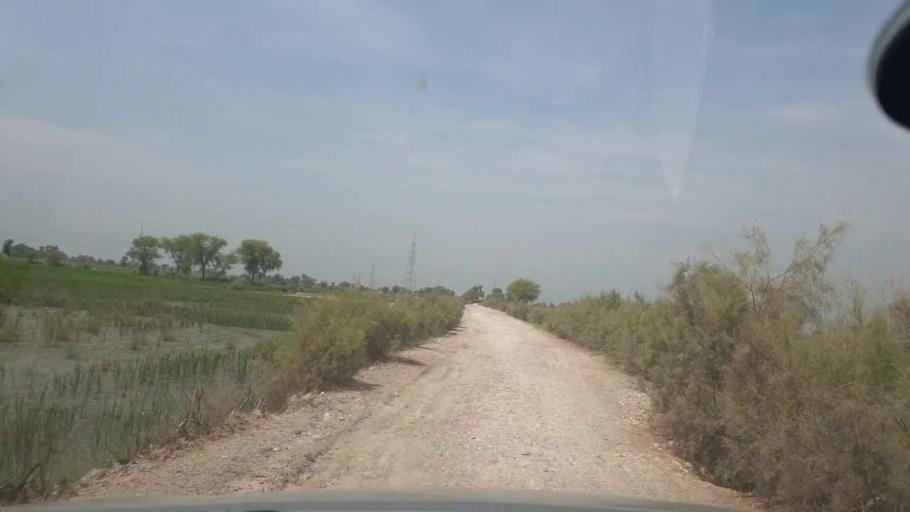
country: PK
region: Sindh
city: Thul
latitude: 28.1791
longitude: 68.6190
